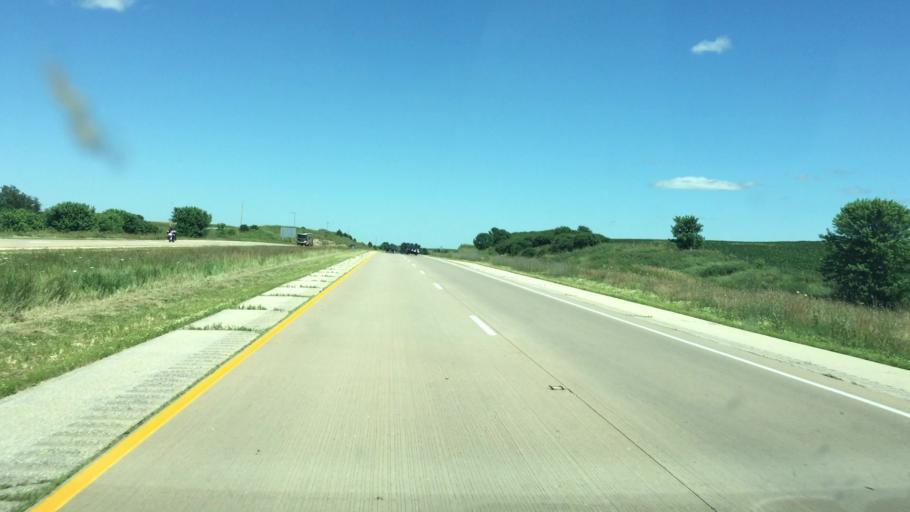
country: US
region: Wisconsin
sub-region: Grant County
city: Platteville
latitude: 42.7389
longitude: -90.4026
